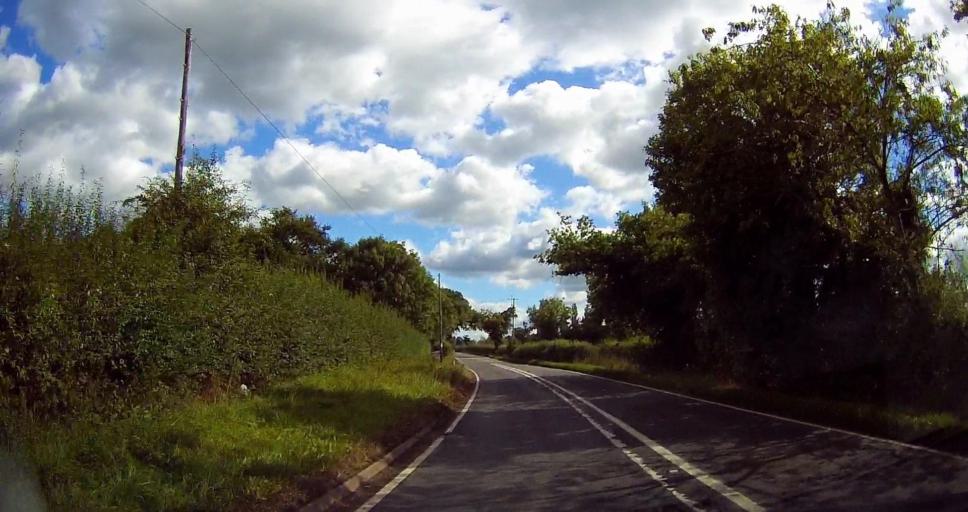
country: GB
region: England
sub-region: Cheshire East
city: Chorlton
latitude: 52.9858
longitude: -2.4581
